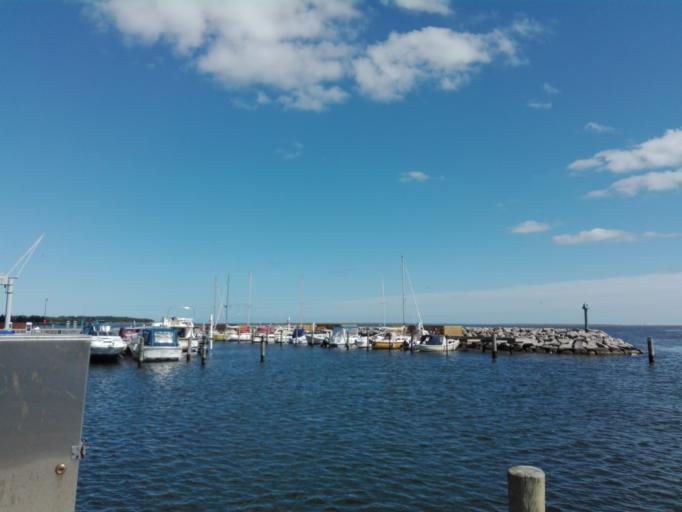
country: DK
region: Central Jutland
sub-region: Norddjurs Kommune
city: Allingabro
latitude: 56.6103
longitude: 10.3057
